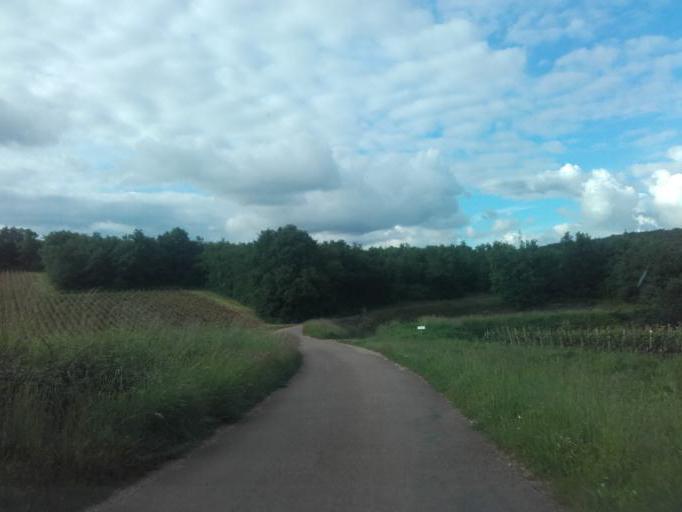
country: FR
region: Bourgogne
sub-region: Departement de Saone-et-Loire
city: Rully
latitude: 46.8439
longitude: 4.7366
